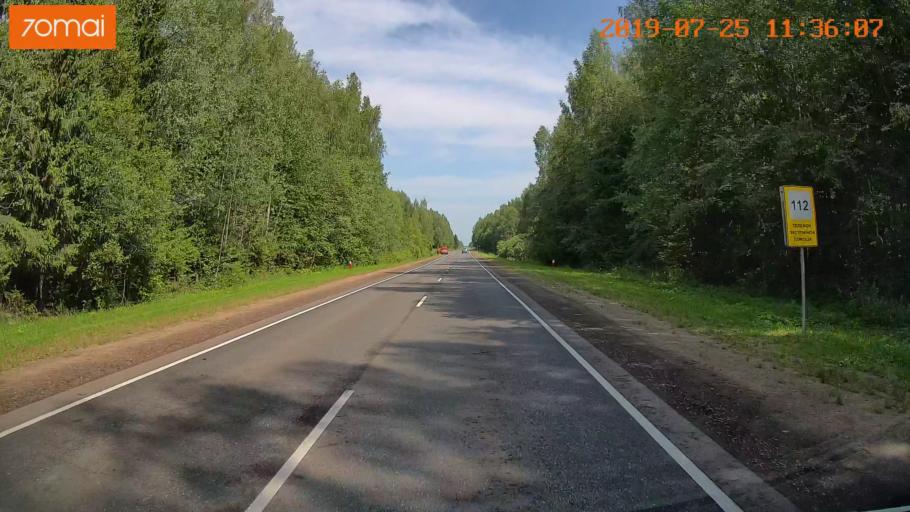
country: RU
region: Ivanovo
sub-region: Privolzhskiy Rayon
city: Ples
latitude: 57.4195
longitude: 41.4424
